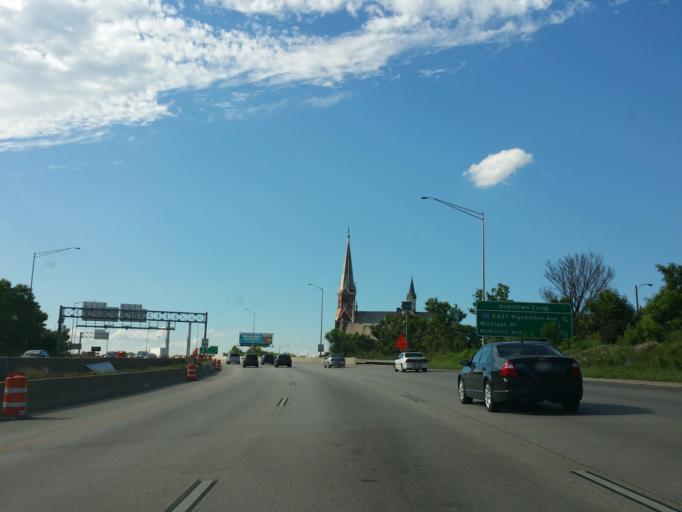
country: US
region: Wisconsin
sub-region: Milwaukee County
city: Milwaukee
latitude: 43.0174
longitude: -87.9161
